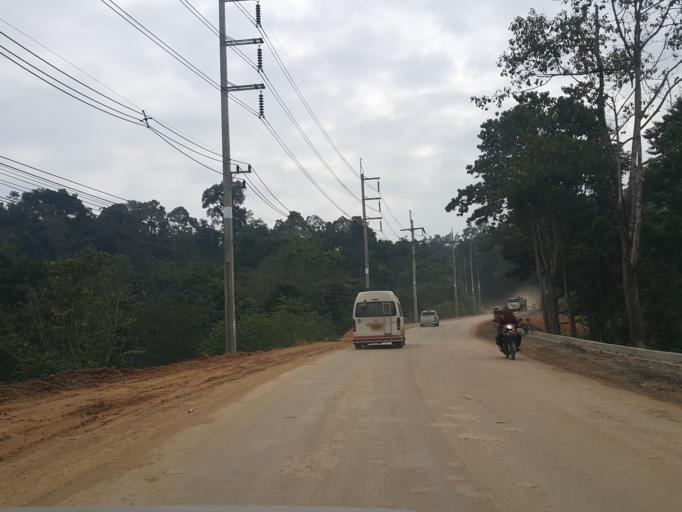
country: TH
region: Chiang Mai
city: Mae Taeng
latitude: 19.1413
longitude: 98.6986
